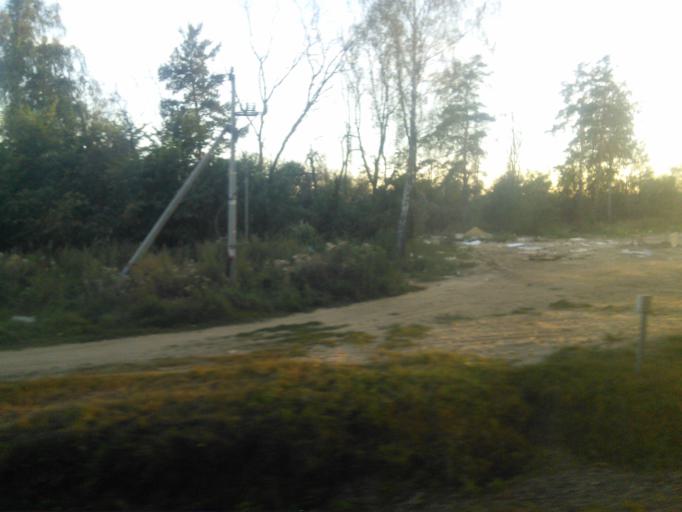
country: RU
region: Moskovskaya
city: Elektrougli
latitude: 55.7388
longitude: 38.1718
